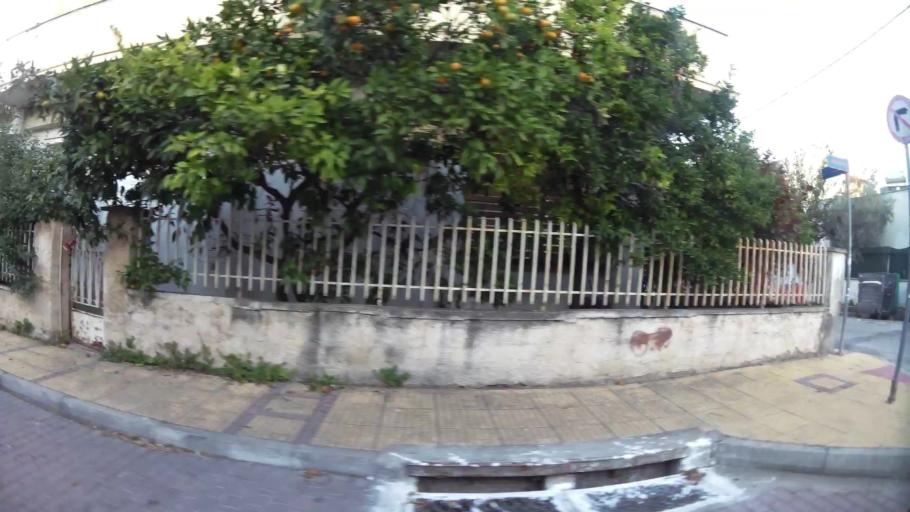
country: GR
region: Attica
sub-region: Nomarchia Athinas
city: Lykovrysi
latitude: 38.0669
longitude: 23.7868
